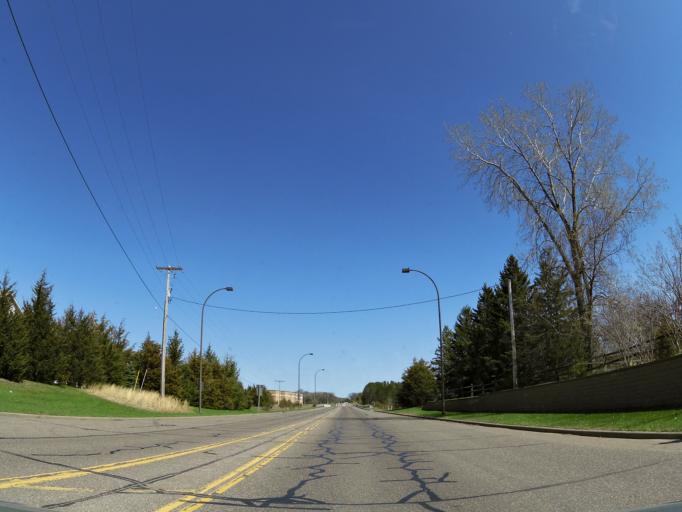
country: US
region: Wisconsin
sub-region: Saint Croix County
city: Hudson
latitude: 44.9585
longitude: -92.6973
